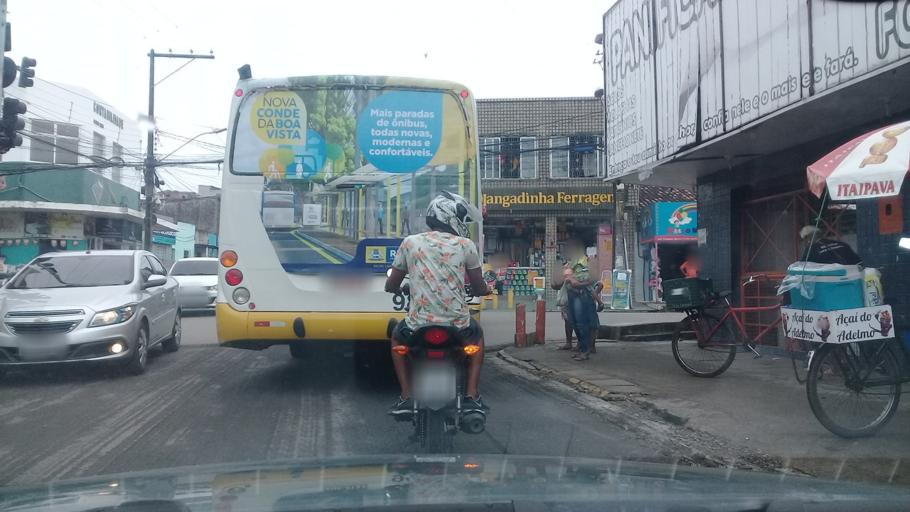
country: BR
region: Pernambuco
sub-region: Jaboatao Dos Guararapes
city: Jaboatao dos Guararapes
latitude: -8.0910
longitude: -34.9735
